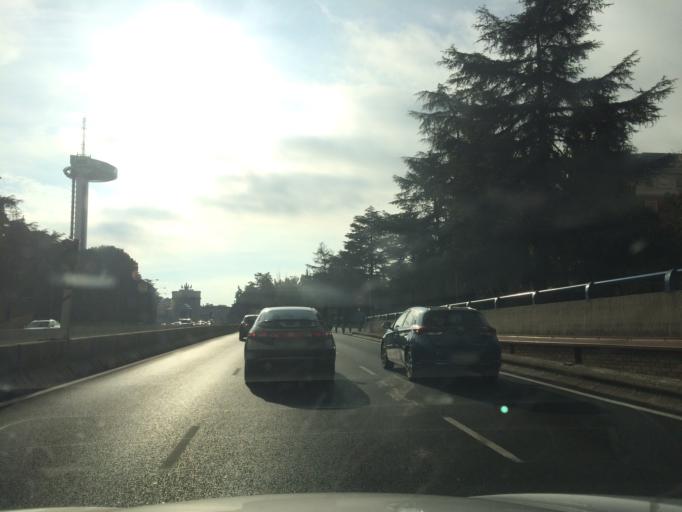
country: ES
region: Madrid
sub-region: Provincia de Madrid
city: Moncloa-Aravaca
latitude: 40.4388
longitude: -3.7253
